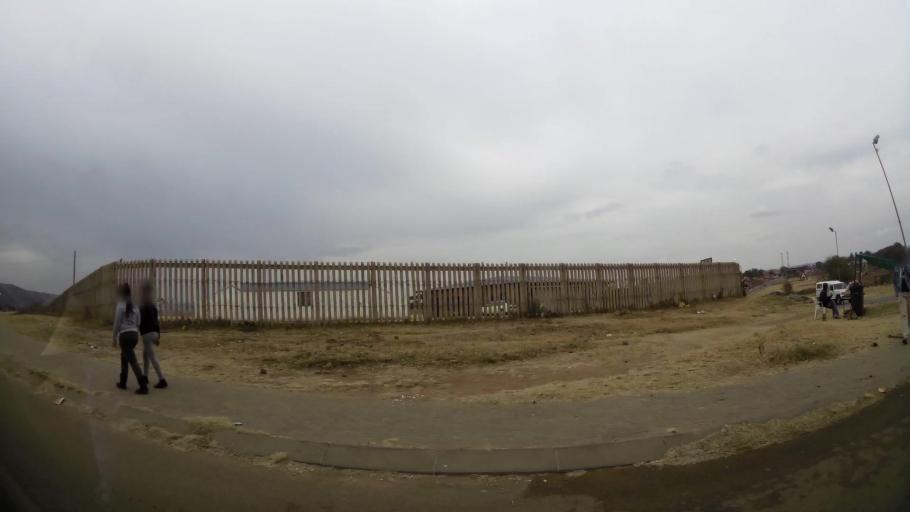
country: ZA
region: Gauteng
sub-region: City of Tshwane Metropolitan Municipality
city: Pretoria
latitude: -25.7065
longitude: 28.3456
